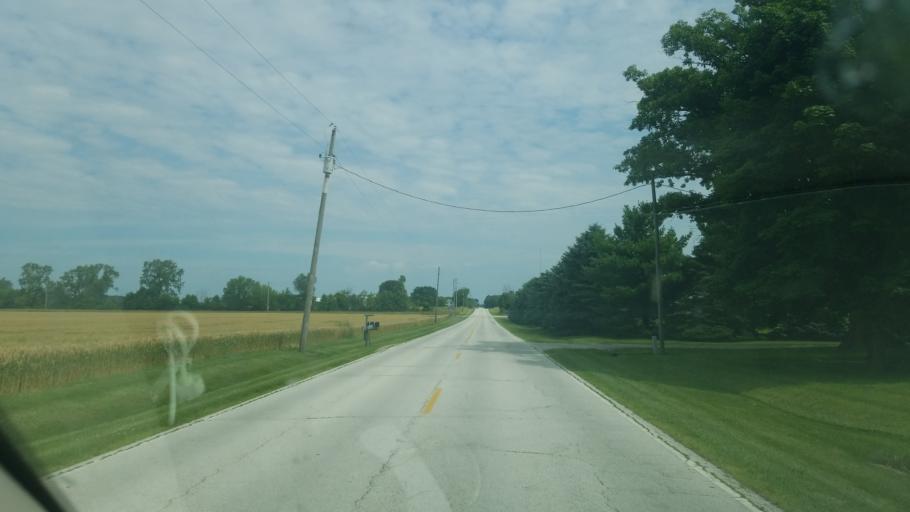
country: US
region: Ohio
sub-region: Seneca County
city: Fostoria
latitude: 41.0916
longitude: -83.4784
